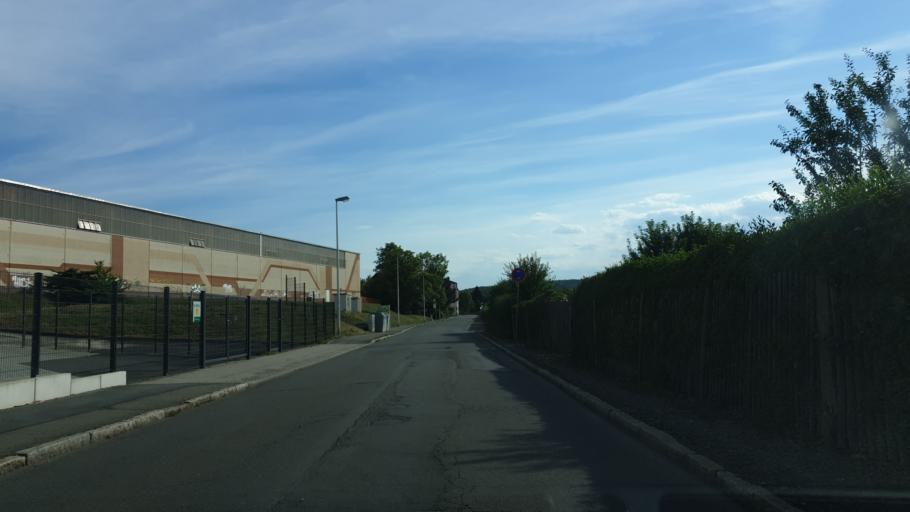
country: DE
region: Thuringia
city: Gera
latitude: 50.8419
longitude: 12.0812
